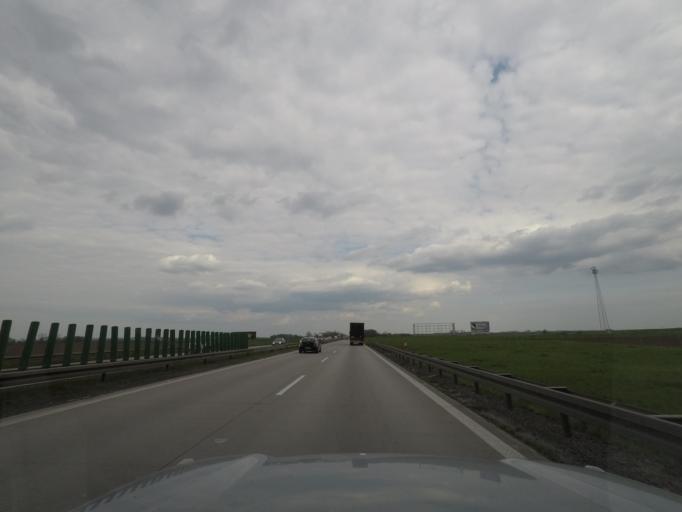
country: PL
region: Lower Silesian Voivodeship
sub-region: Powiat wroclawski
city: Katy Wroclawskie
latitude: 51.0344
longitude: 16.8157
